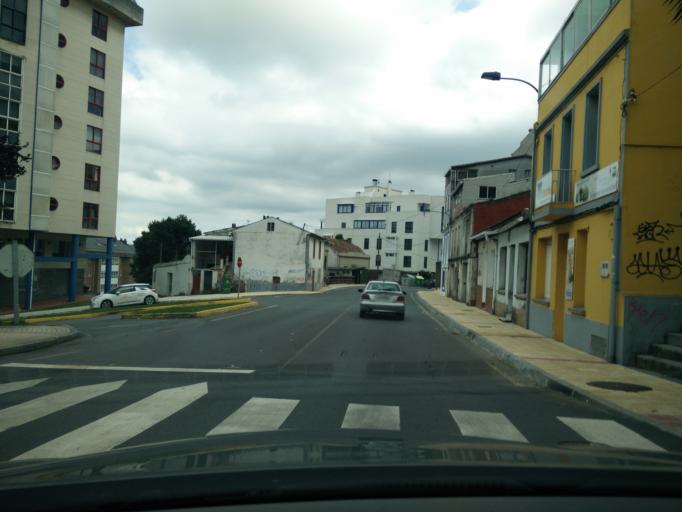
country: ES
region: Galicia
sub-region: Provincia da Coruna
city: Culleredo
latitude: 43.3248
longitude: -8.3846
